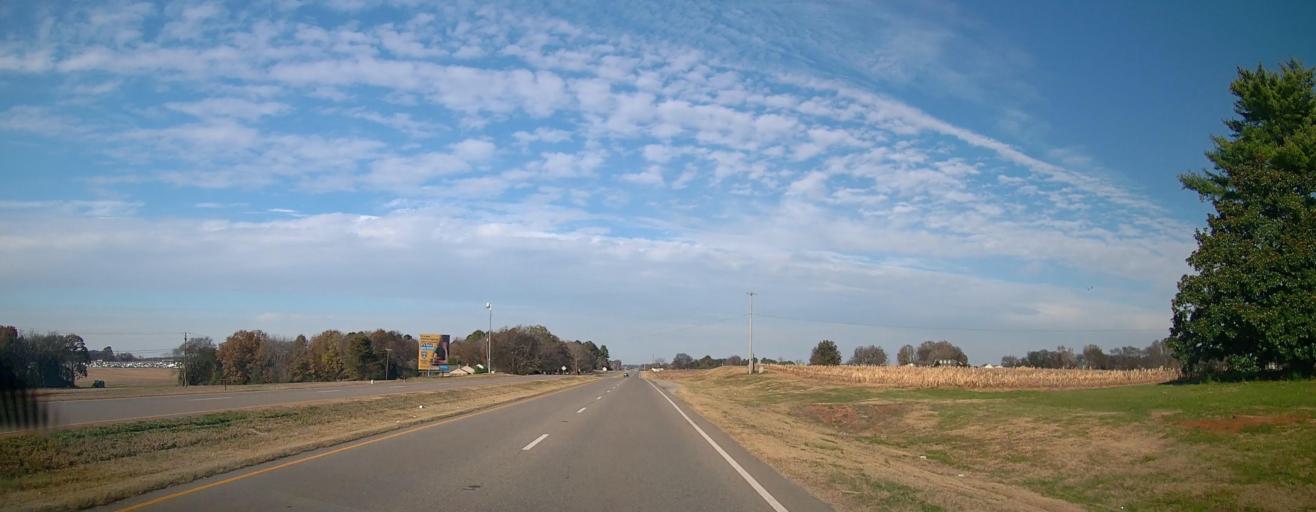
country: US
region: Alabama
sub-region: Morgan County
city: Decatur
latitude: 34.6342
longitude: -86.9507
